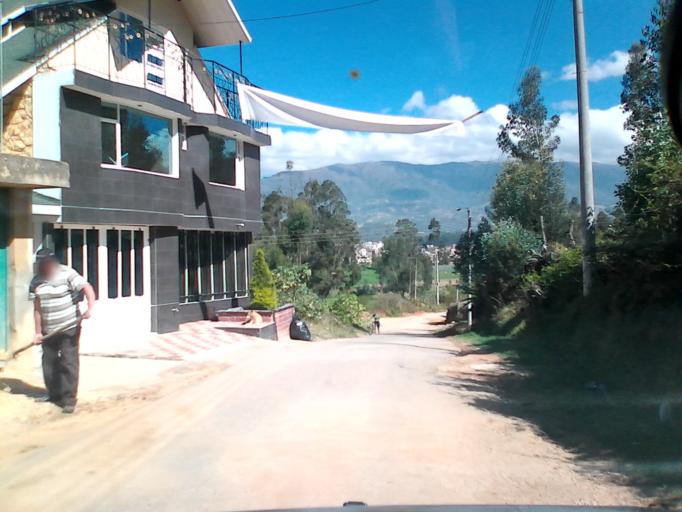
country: CO
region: Boyaca
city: Duitama
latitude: 5.7995
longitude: -73.0147
